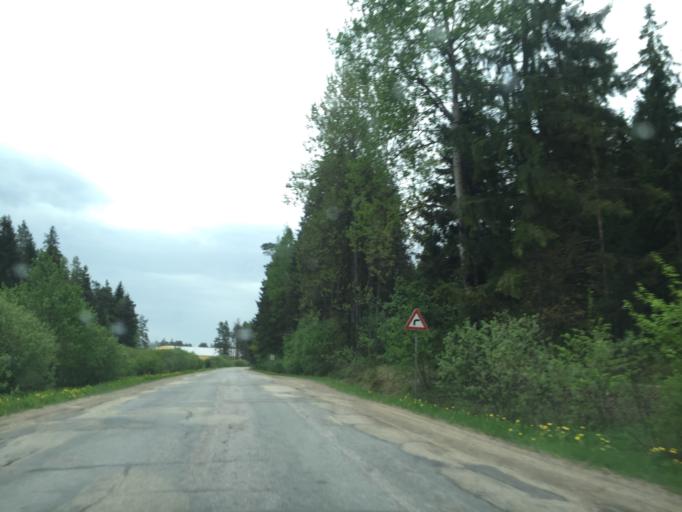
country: LV
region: Ogre
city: Ogre
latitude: 56.8283
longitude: 24.5944
